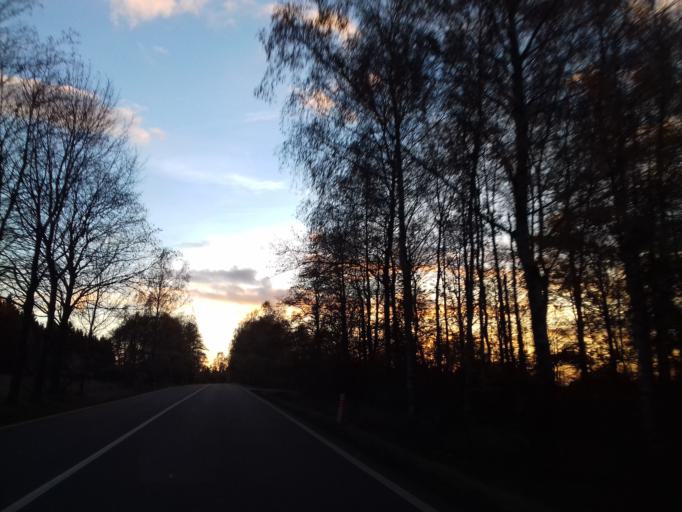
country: CZ
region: Pardubicky
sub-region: Okres Chrudim
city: Hlinsko
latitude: 49.7401
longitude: 15.8815
